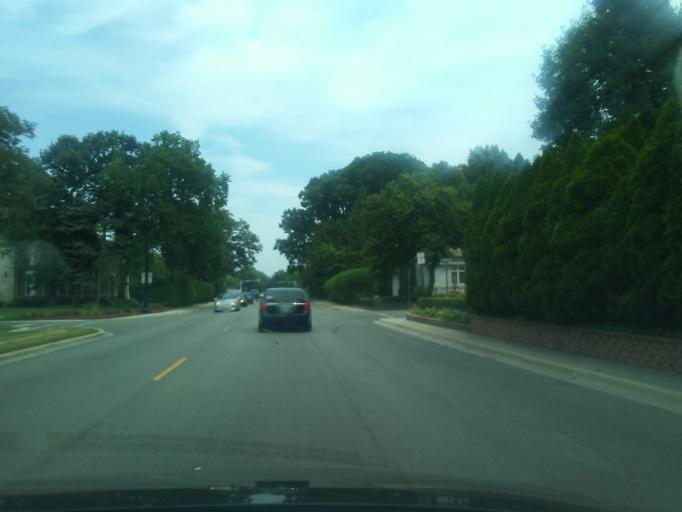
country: US
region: Illinois
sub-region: Cook County
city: Lincolnwood
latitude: 42.0045
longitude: -87.7510
